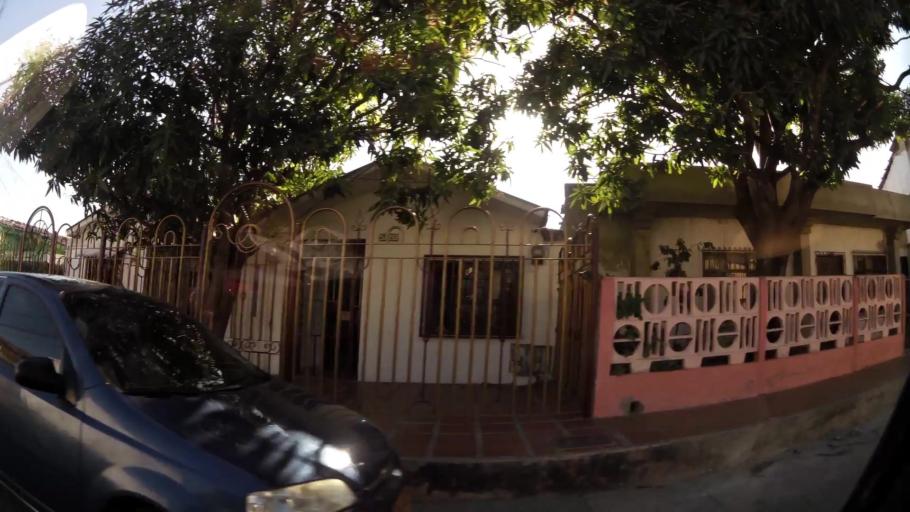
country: CO
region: Atlantico
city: Barranquilla
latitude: 10.9922
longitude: -74.7850
